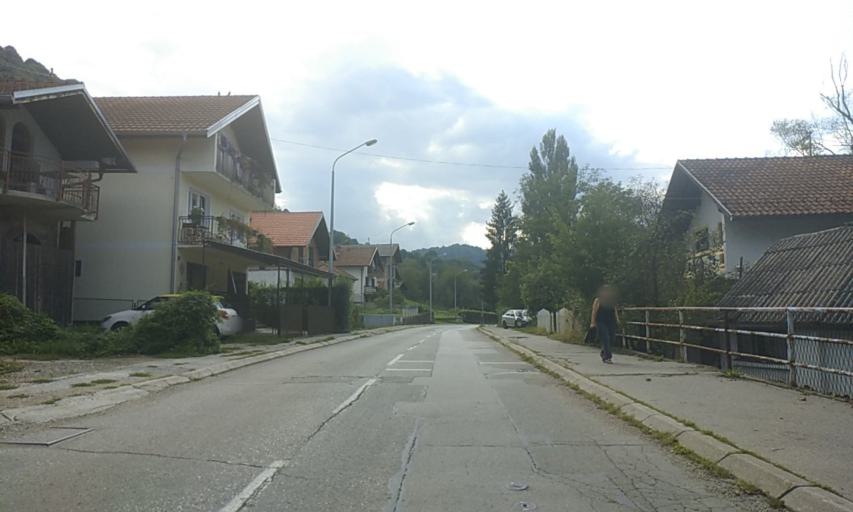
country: BA
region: Republika Srpska
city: Hiseti
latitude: 44.7514
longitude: 17.1732
